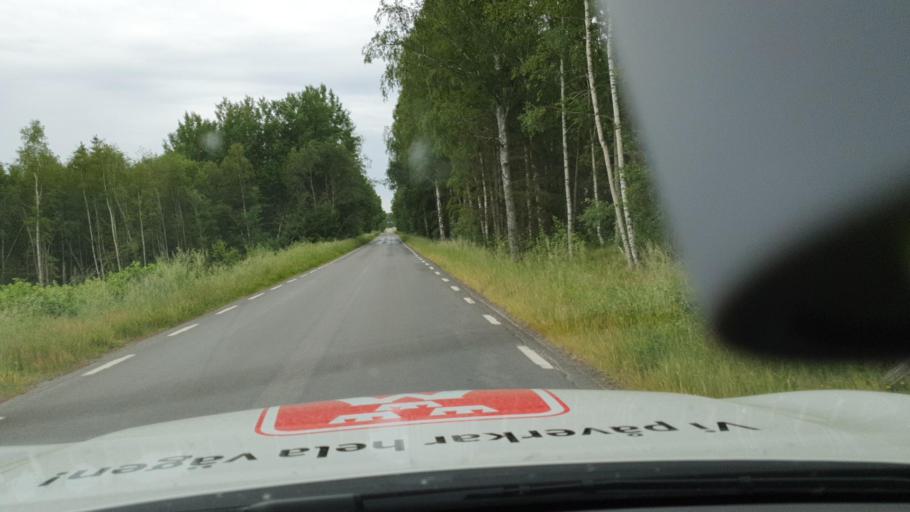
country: SE
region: Vaestra Goetaland
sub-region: Tibro Kommun
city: Tibro
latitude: 58.3390
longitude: 14.1051
